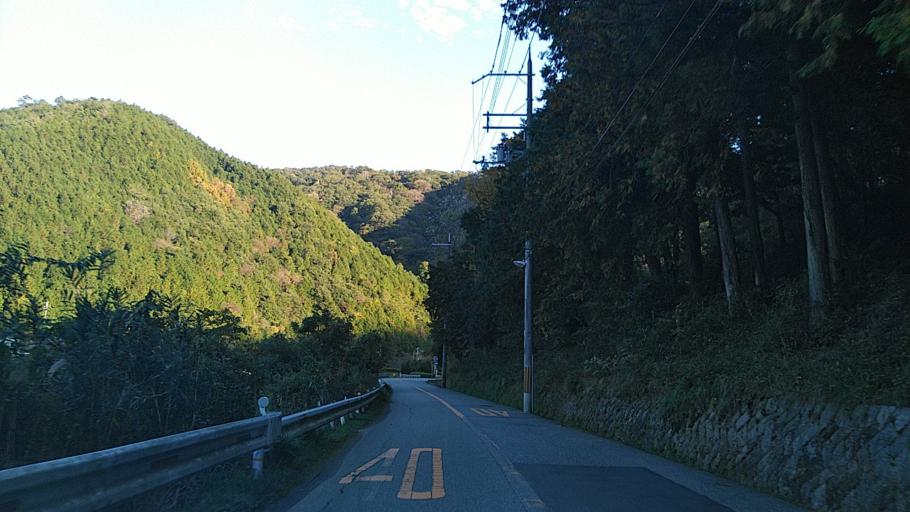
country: JP
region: Osaka
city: Ikeda
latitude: 34.9448
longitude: 135.4091
